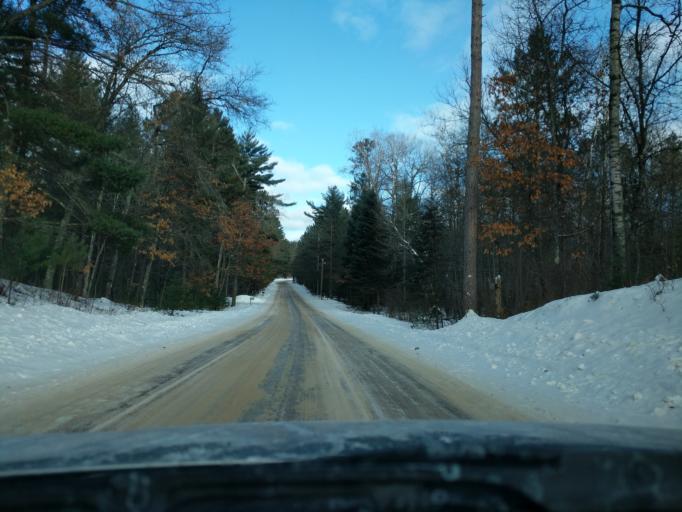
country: US
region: Wisconsin
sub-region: Vilas County
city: Eagle River
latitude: 45.7940
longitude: -89.0765
